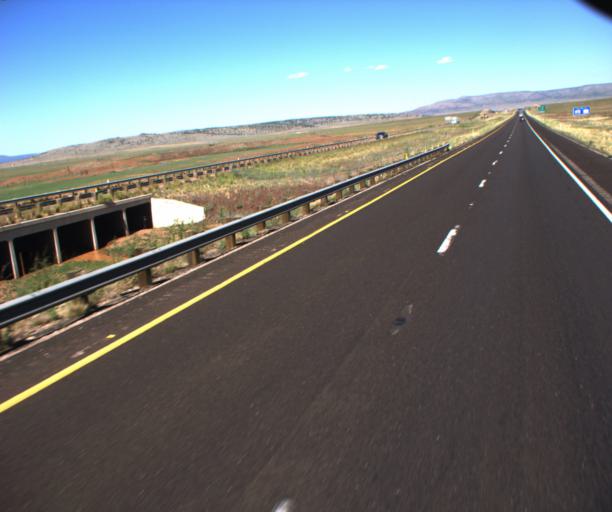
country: US
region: Arizona
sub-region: Yavapai County
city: Paulden
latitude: 35.2974
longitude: -112.8329
